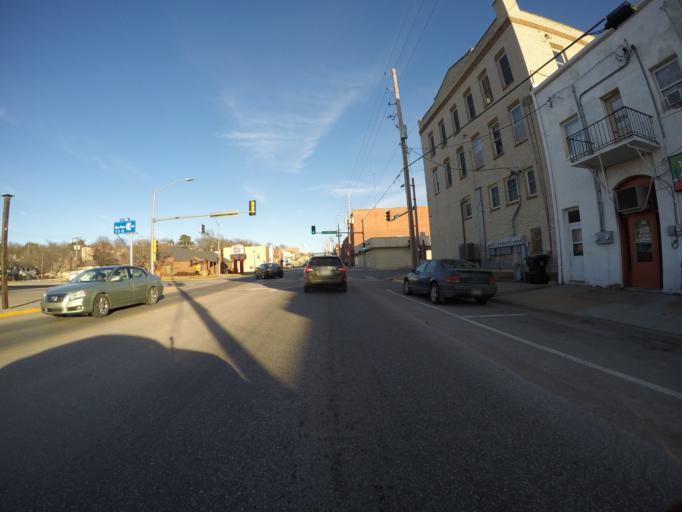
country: US
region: Kansas
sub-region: Marshall County
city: Marysville
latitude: 39.8421
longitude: -96.6486
